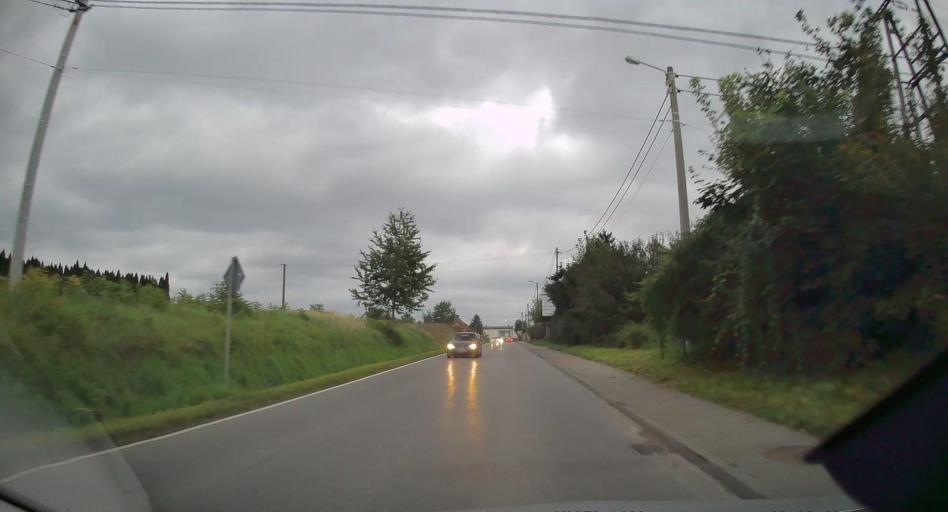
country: PL
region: Lesser Poland Voivodeship
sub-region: Powiat krakowski
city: Slomniki
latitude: 50.1378
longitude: 20.1120
